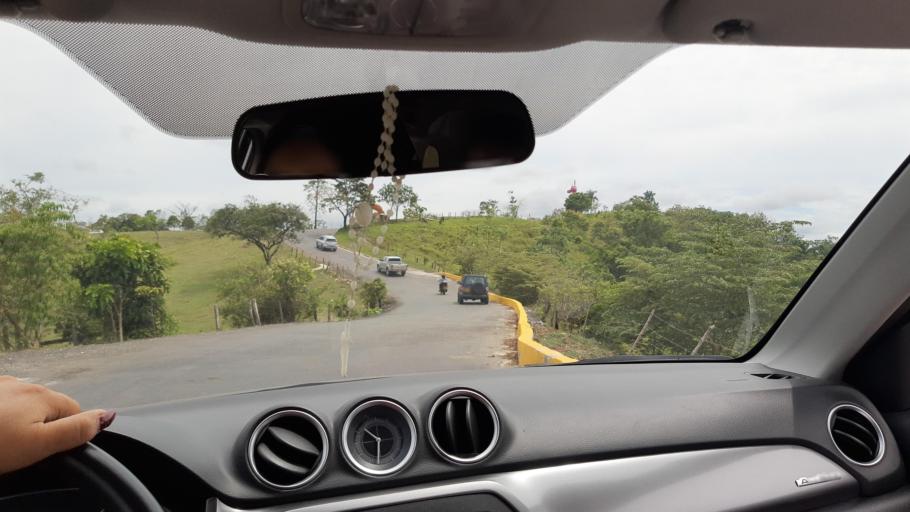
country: CO
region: Antioquia
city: Puerto Triunfo
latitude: 5.9041
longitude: -74.7203
